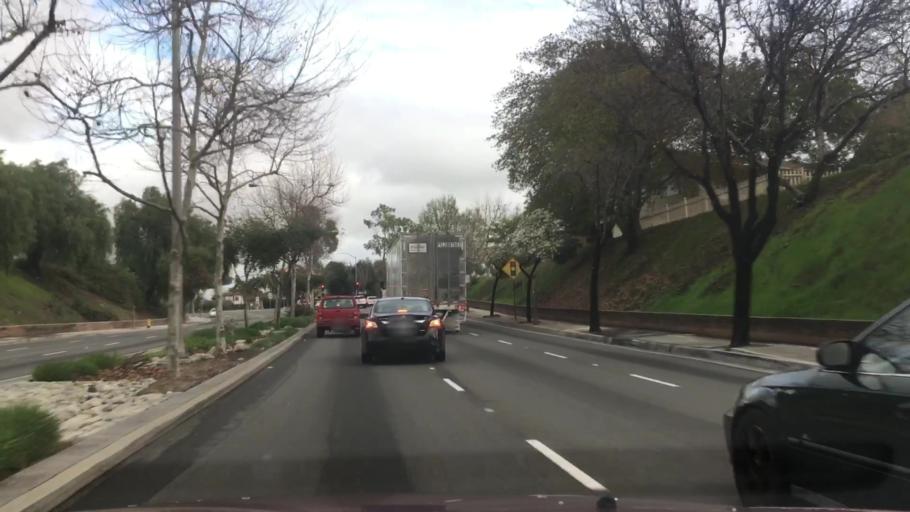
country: US
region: California
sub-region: Los Angeles County
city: La Mirada
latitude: 33.9166
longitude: -118.0076
